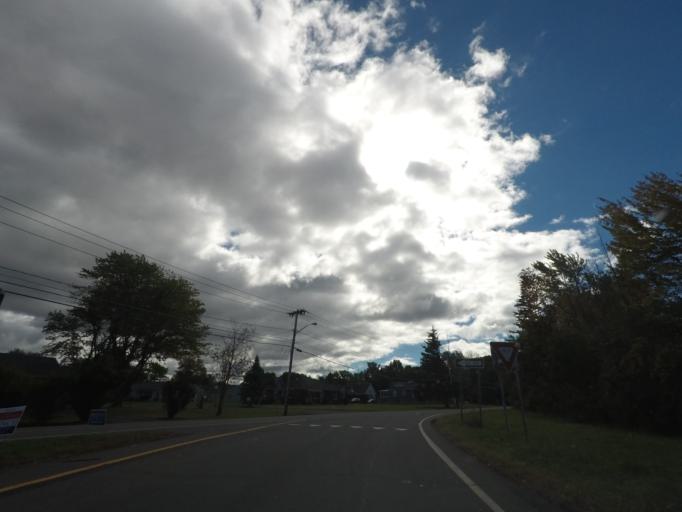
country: US
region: New York
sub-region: Albany County
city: Cohoes
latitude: 42.7843
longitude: -73.7304
